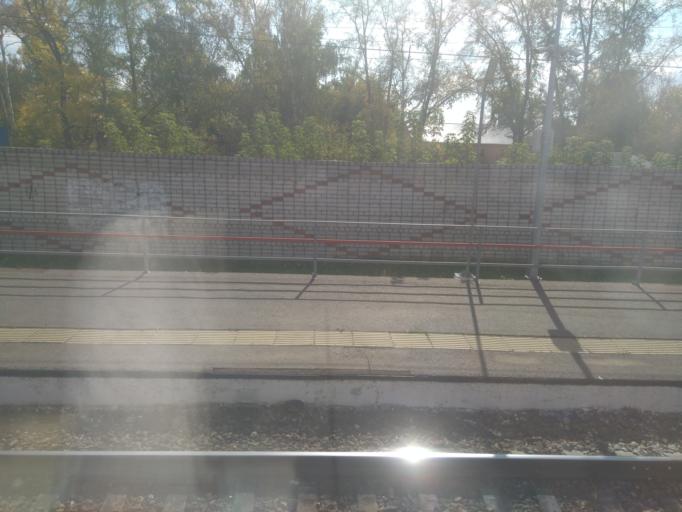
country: RU
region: Tatarstan
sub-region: Zelenodol'skiy Rayon
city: Zelenodolsk
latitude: 55.8420
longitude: 48.5632
